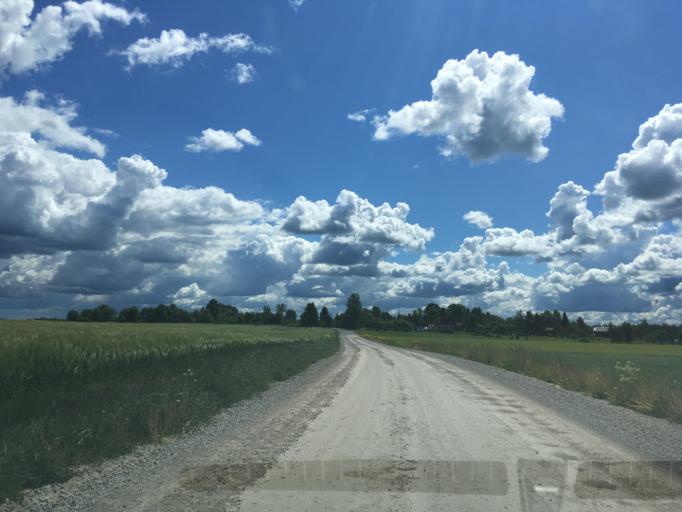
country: EE
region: Harju
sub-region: Nissi vald
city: Turba
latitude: 58.9220
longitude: 24.1596
